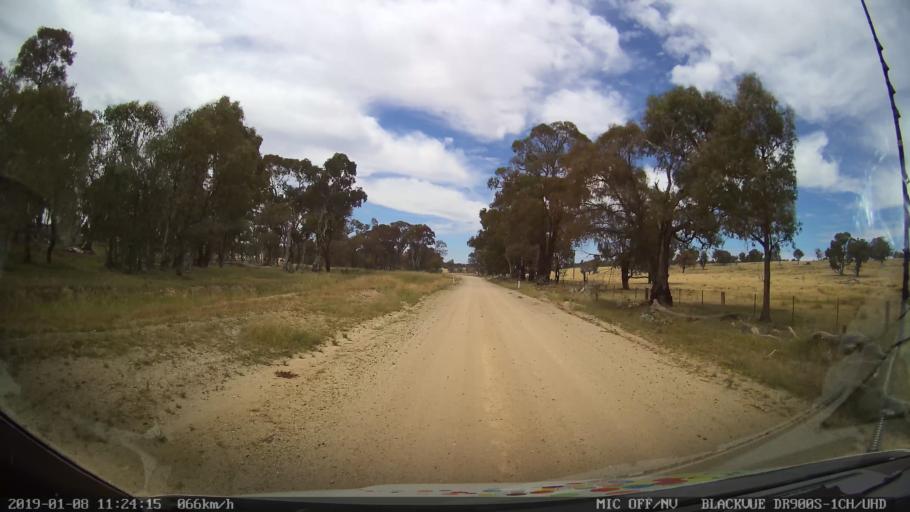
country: AU
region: New South Wales
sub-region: Guyra
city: Guyra
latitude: -30.2628
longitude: 151.5582
